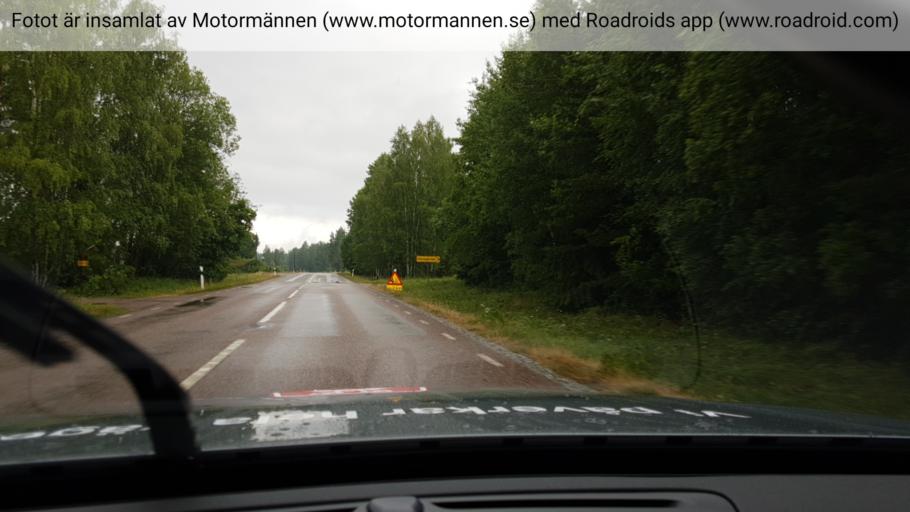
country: SE
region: Vaestmanland
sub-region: Norbergs Kommun
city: Norberg
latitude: 60.0306
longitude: 15.9938
